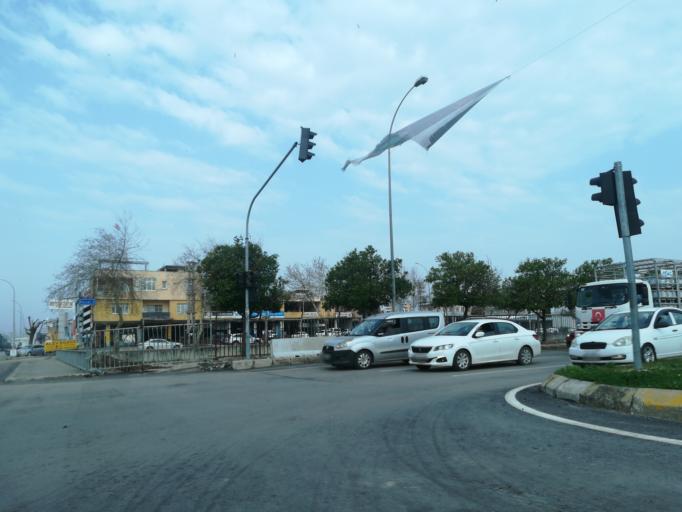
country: TR
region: Adana
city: Yuregir
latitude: 36.9853
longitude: 35.3676
